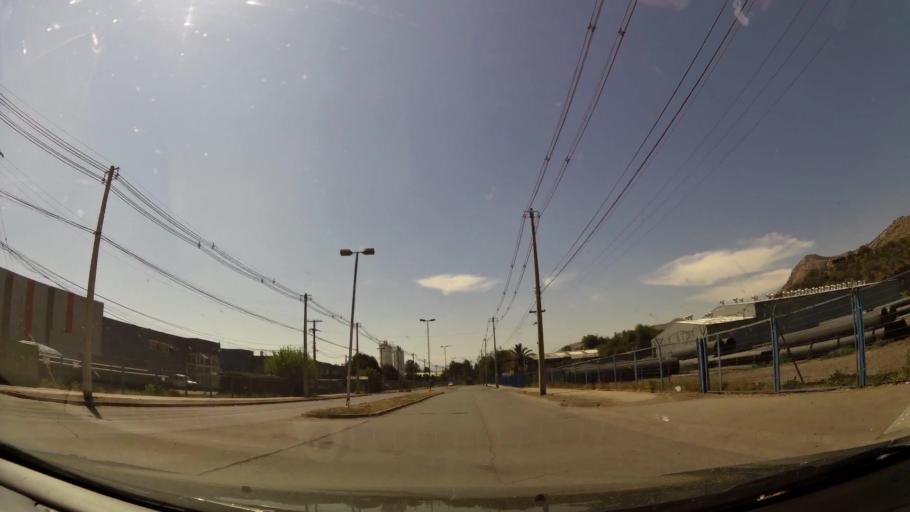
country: CL
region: Santiago Metropolitan
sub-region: Provincia de Santiago
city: Lo Prado
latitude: -33.3866
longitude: -70.7530
